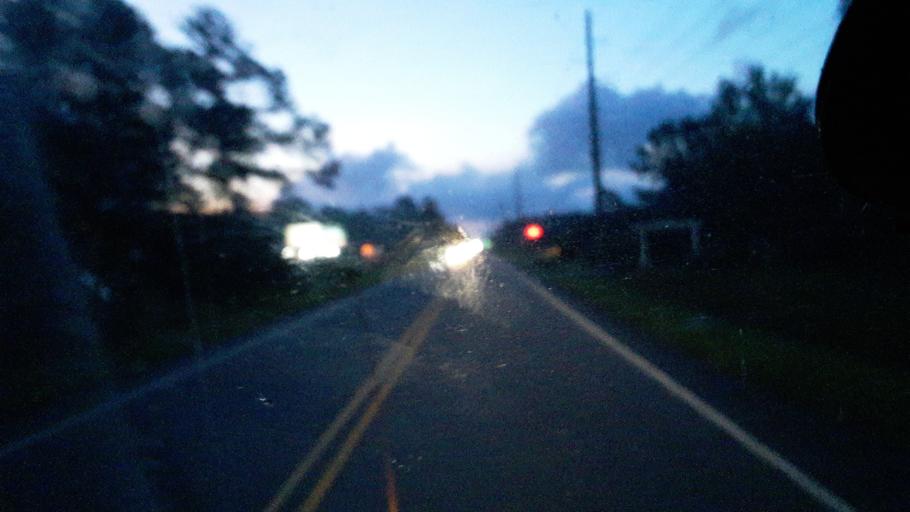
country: US
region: North Carolina
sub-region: Brunswick County
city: Oak Island
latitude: 33.9910
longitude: -78.2102
